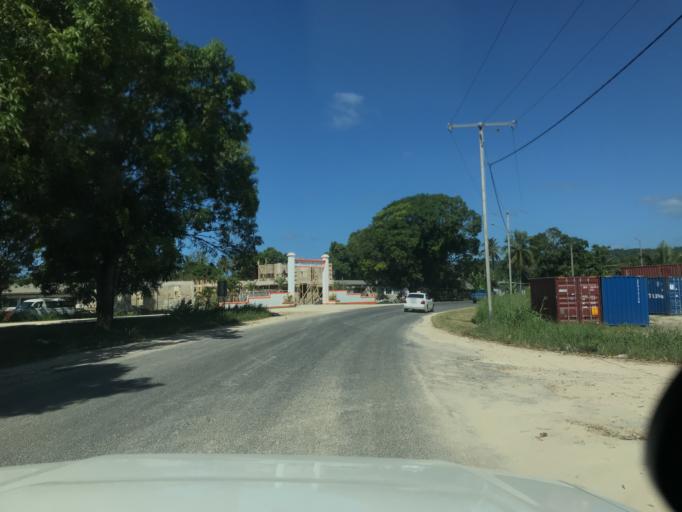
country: VU
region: Sanma
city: Luganville
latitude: -15.5179
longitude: 167.1674
